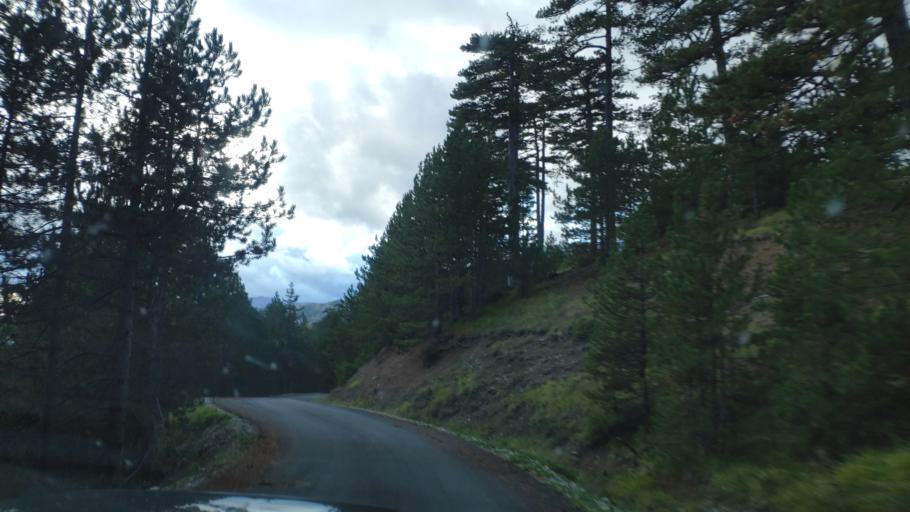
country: AL
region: Korce
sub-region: Rrethi i Kolonjes
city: Erseke
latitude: 40.2942
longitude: 20.8632
